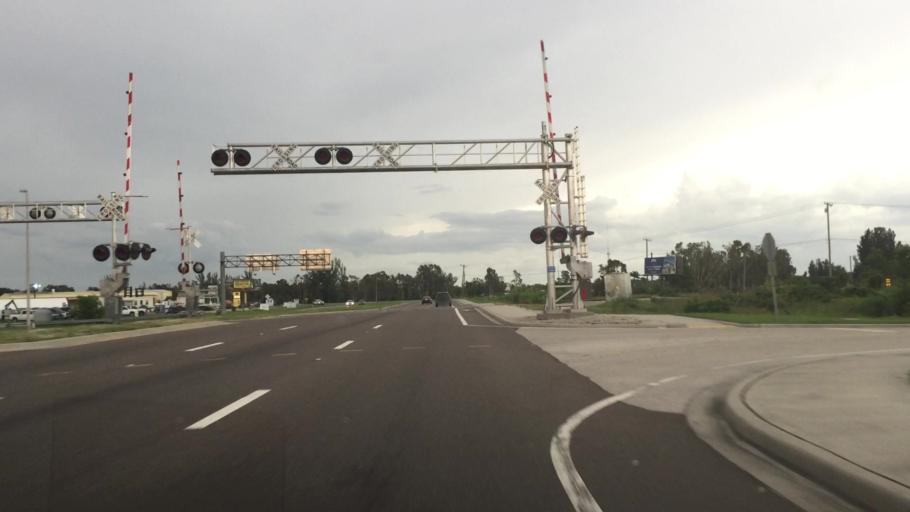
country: US
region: Florida
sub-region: Lee County
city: San Carlos Park
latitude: 26.4939
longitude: -81.8422
